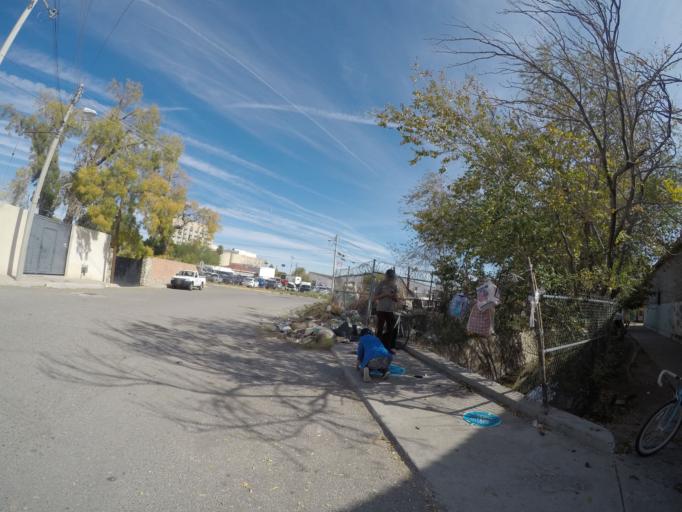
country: MX
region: Chihuahua
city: Ciudad Juarez
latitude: 31.7350
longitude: -106.4520
